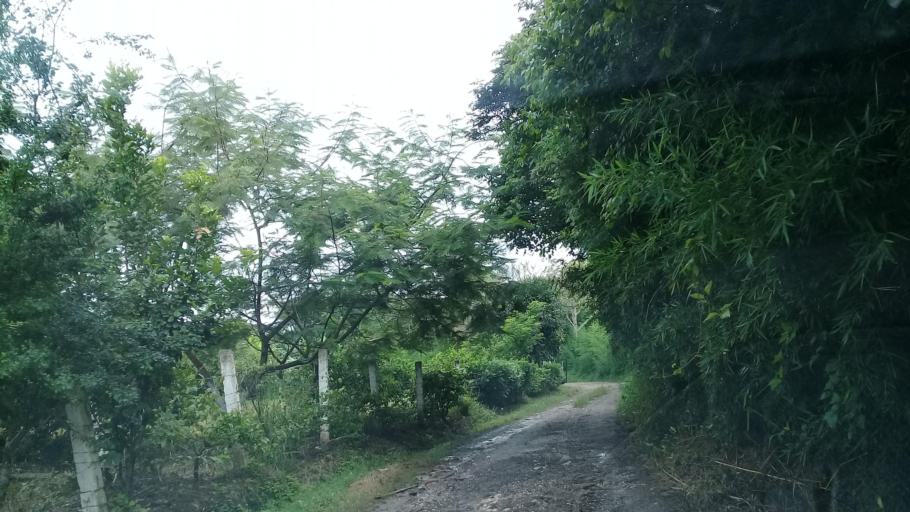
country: MX
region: Veracruz
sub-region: Emiliano Zapata
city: Dos Rios
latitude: 19.4793
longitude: -96.8090
